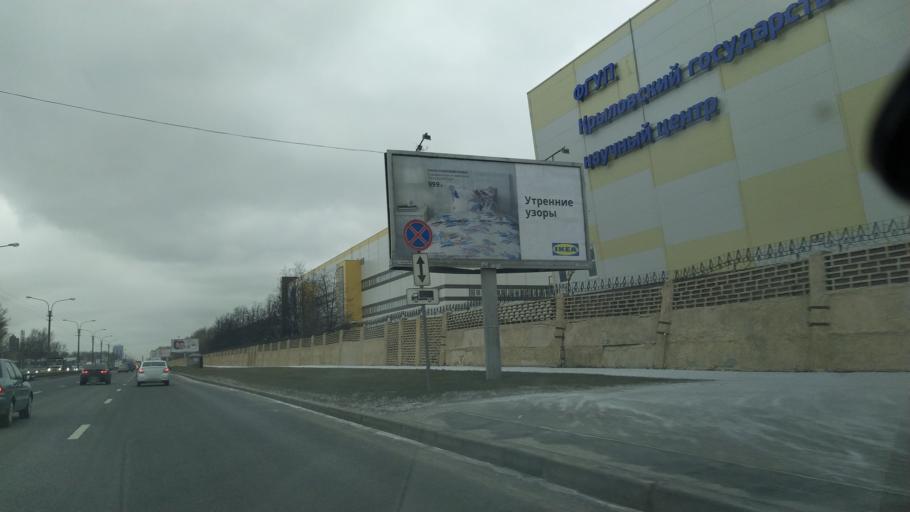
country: RU
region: St.-Petersburg
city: Shushary
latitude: 59.8203
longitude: 30.3644
